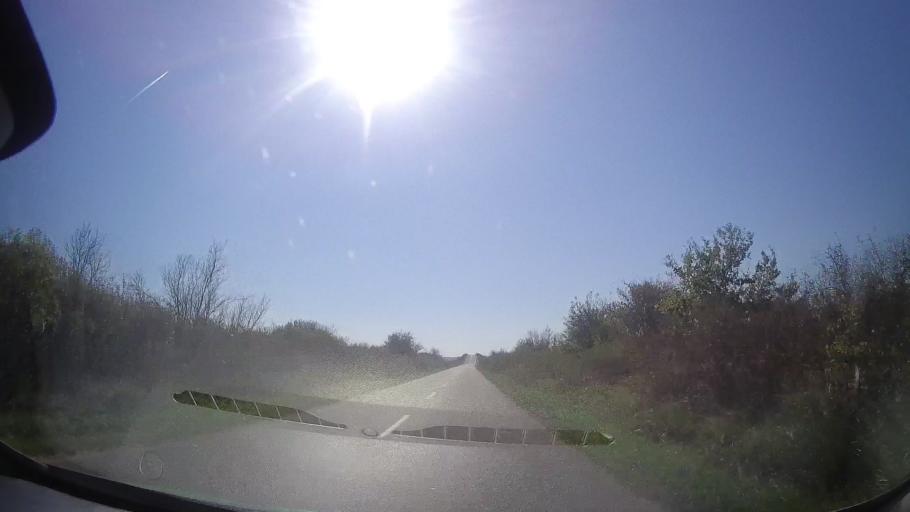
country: RO
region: Timis
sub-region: Comuna Bethausen
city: Bethausen
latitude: 45.8203
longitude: 21.9599
